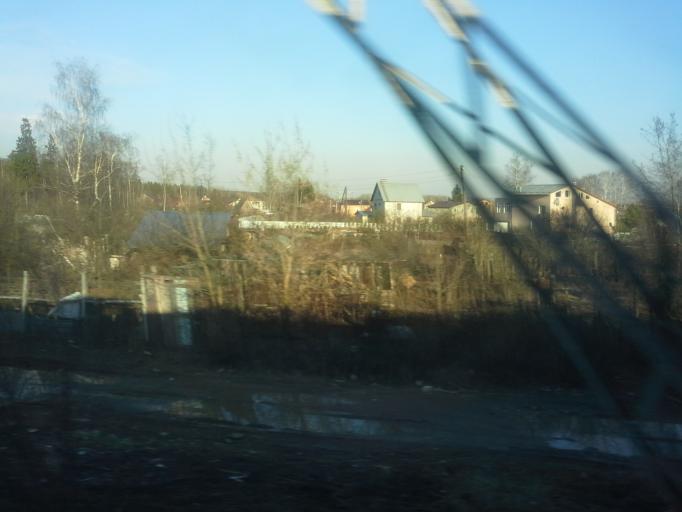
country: RU
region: Moskovskaya
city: Nekrasovskiy
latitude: 56.0953
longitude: 37.5068
